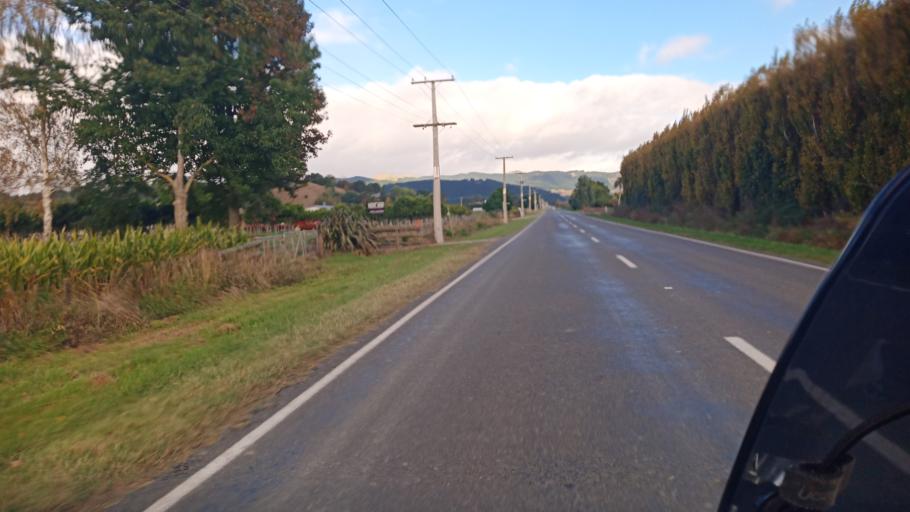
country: NZ
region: Gisborne
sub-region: Gisborne District
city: Gisborne
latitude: -38.6315
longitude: 177.8852
